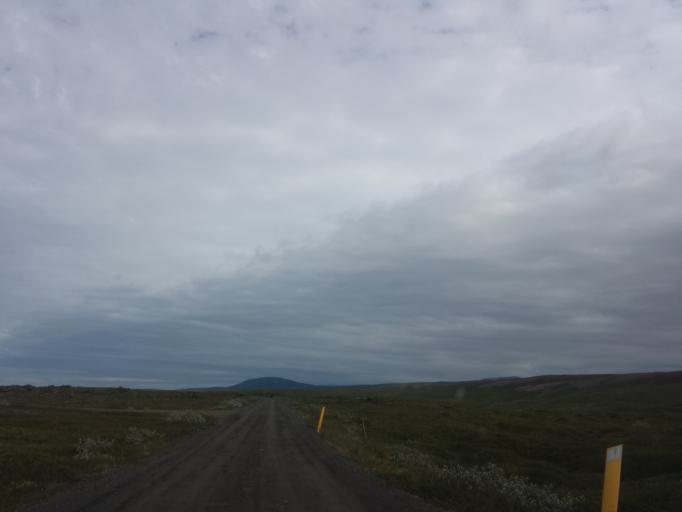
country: IS
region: Northeast
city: Husavik
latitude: 65.9358
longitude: -17.4319
